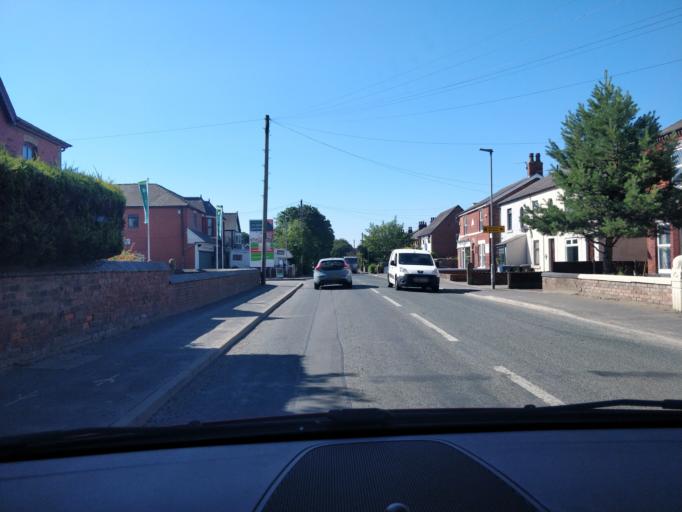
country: GB
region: England
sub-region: Lancashire
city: Tarleton
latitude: 53.6974
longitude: -2.8381
